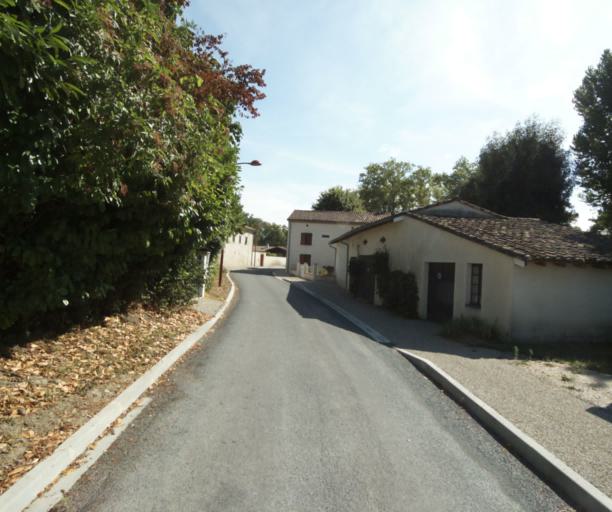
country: FR
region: Midi-Pyrenees
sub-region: Departement de la Haute-Garonne
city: Revel
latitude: 43.4980
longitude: 1.9697
